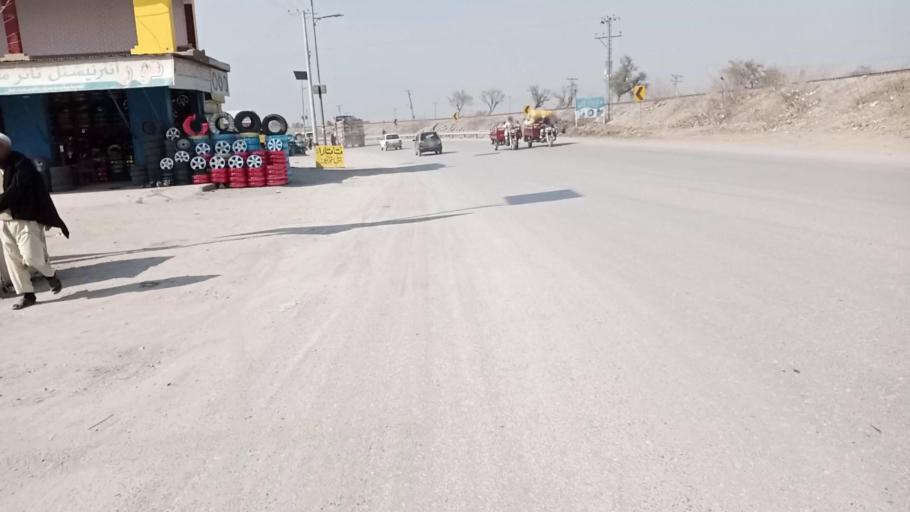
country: PK
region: Khyber Pakhtunkhwa
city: Peshawar
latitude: 34.0010
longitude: 71.3987
